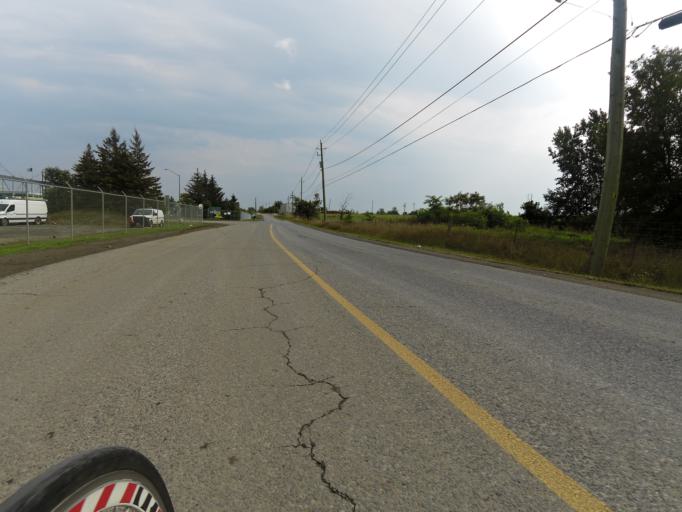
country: CA
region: Ontario
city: Bells Corners
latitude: 45.2340
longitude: -75.7746
